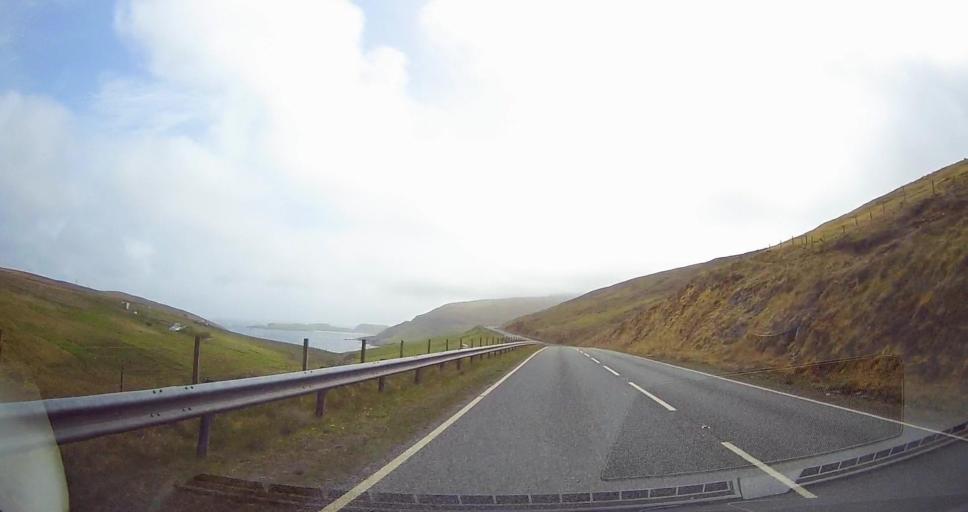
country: GB
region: Scotland
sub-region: Shetland Islands
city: Sandwick
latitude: 60.0003
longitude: -1.2800
